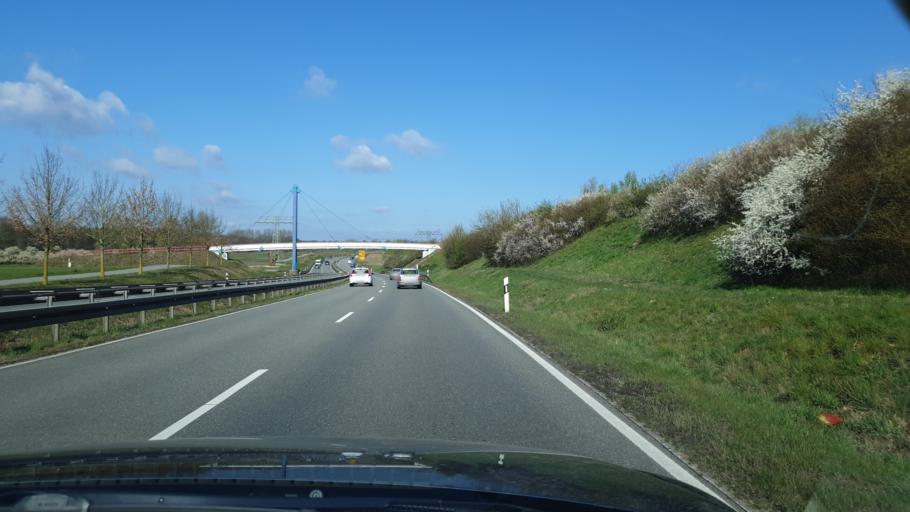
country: DE
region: Mecklenburg-Vorpommern
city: Neumuehle
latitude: 53.6390
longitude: 11.3532
